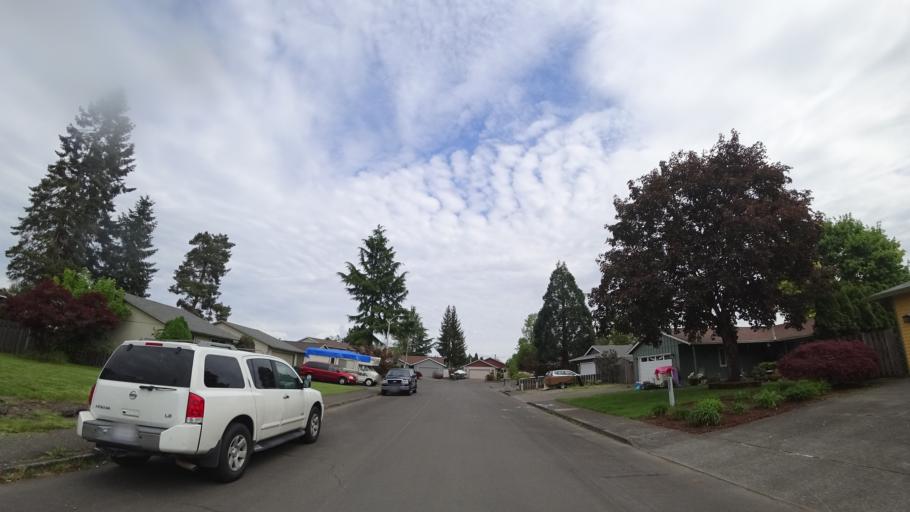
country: US
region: Oregon
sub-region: Washington County
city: Hillsboro
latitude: 45.4963
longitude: -122.9640
